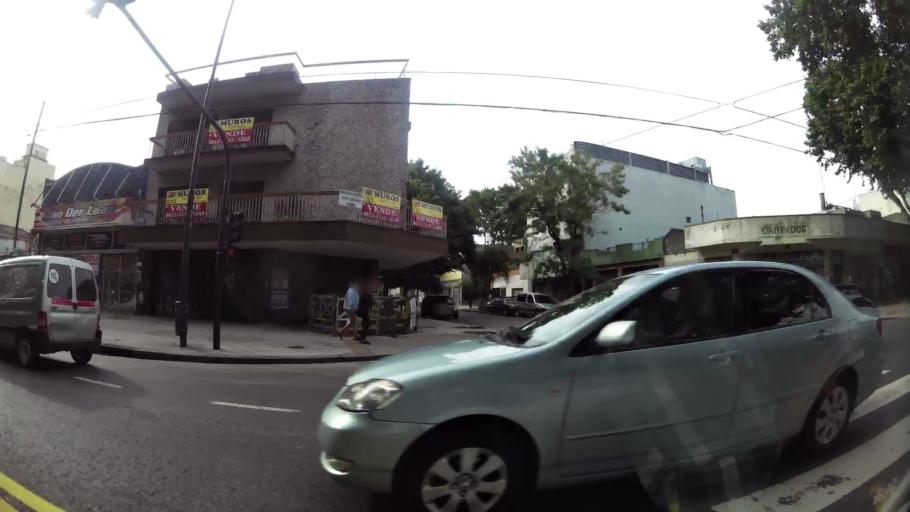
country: AR
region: Buenos Aires F.D.
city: Villa Lugano
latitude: -34.6449
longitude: -58.4650
